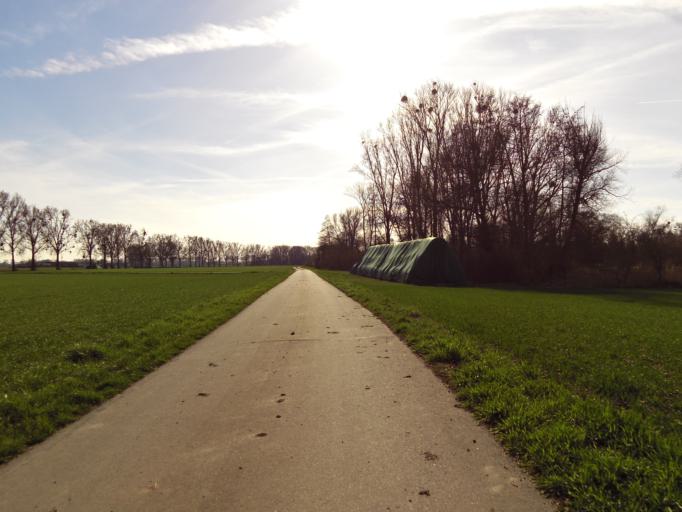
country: DE
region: Hesse
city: Biebesheim
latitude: 49.7905
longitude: 8.4350
